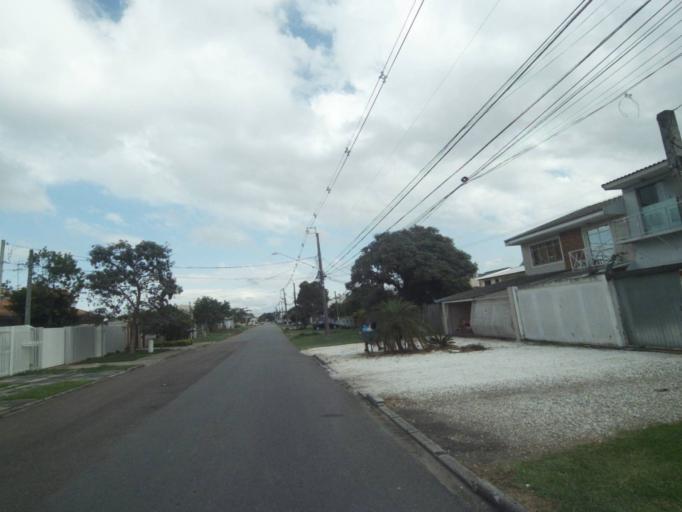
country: BR
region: Parana
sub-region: Pinhais
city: Pinhais
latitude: -25.4502
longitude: -49.2056
